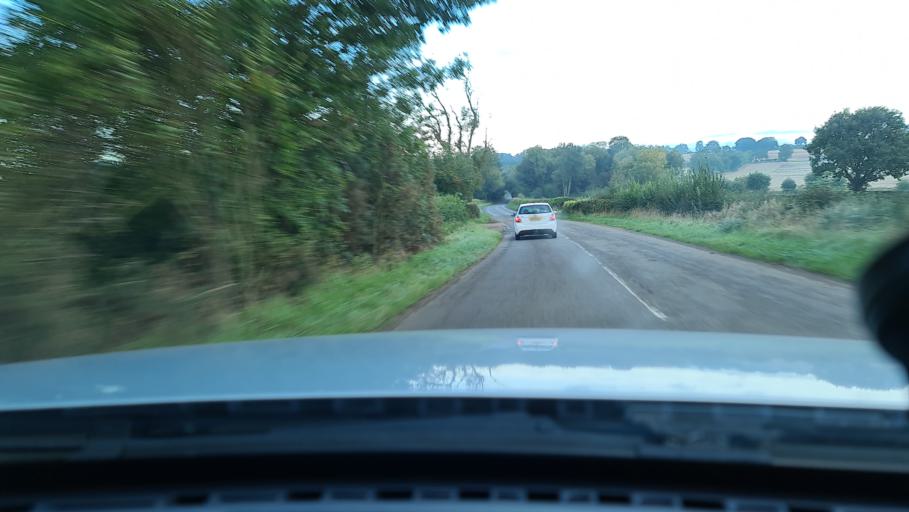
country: GB
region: England
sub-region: Oxfordshire
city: Hanwell
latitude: 52.0961
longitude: -1.3520
